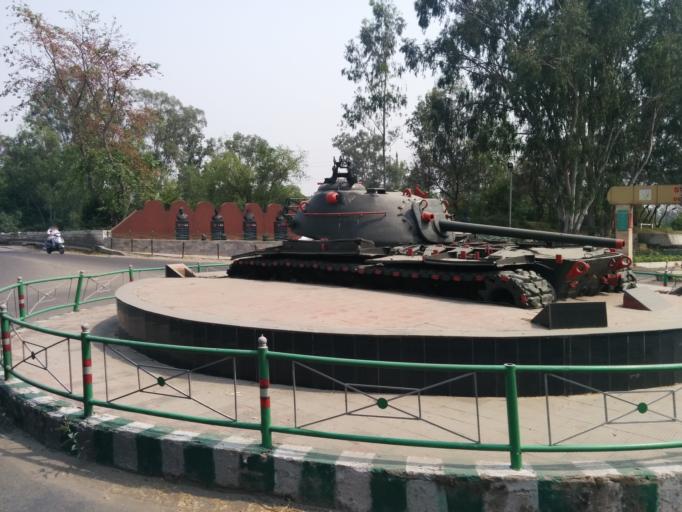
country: IN
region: Punjab
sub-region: Pathankot
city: Pathankot
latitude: 32.2744
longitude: 75.6270
